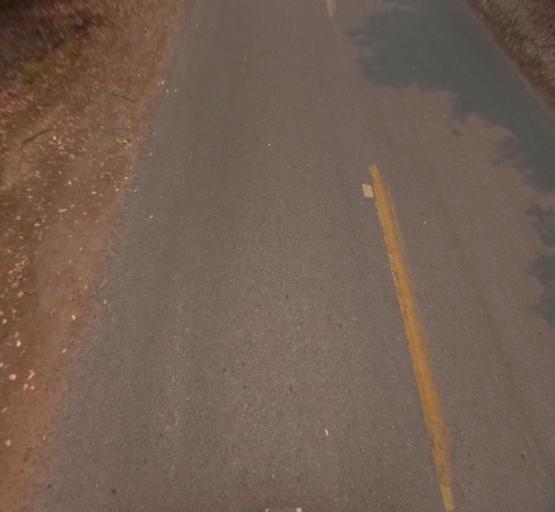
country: US
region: California
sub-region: Madera County
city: Madera Acres
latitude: 37.0227
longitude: -120.0686
